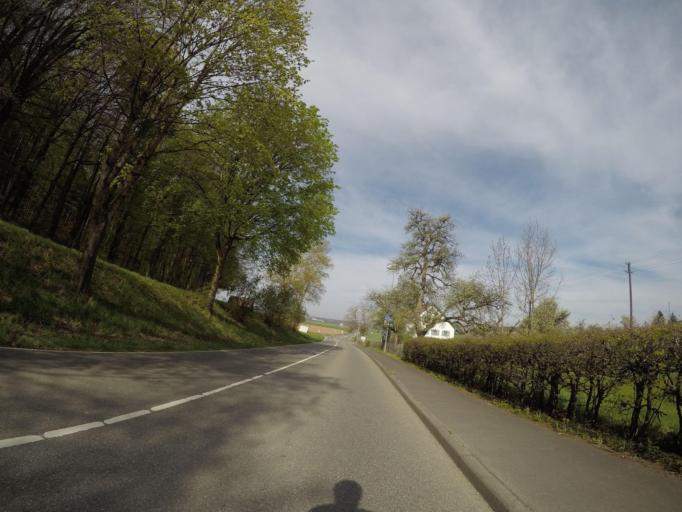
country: DE
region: Baden-Wuerttemberg
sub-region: Tuebingen Region
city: Allmannsweiler
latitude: 48.0088
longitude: 9.5597
